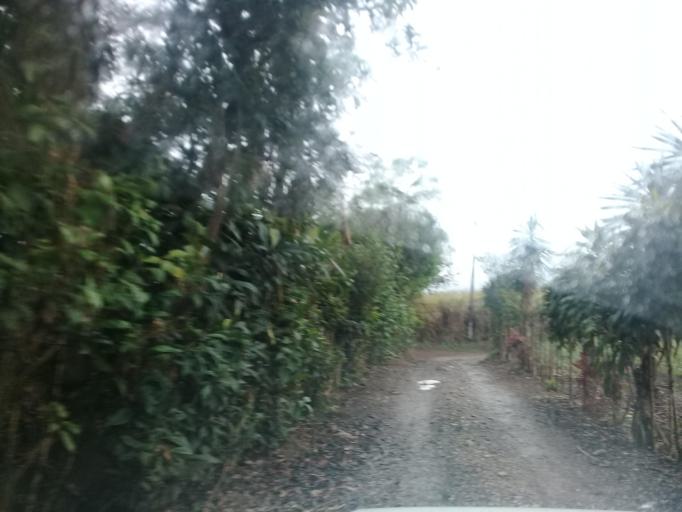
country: MX
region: Veracruz
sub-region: Amatlan de los Reyes
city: Centro de Readaptacion Social
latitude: 18.8195
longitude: -96.9445
